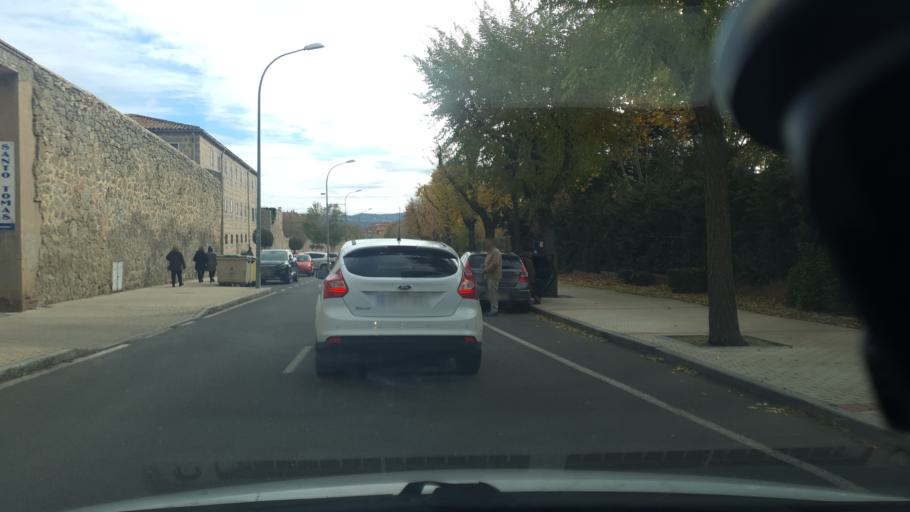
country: ES
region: Castille and Leon
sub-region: Provincia de Avila
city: Avila
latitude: 40.6499
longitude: -4.6897
